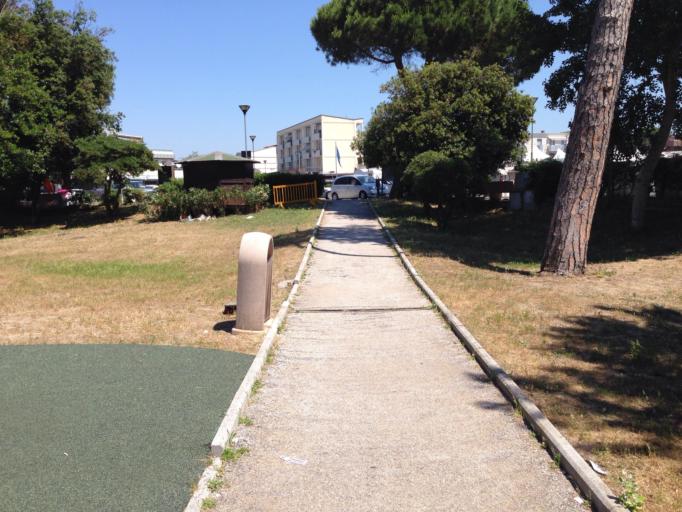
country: IT
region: Tuscany
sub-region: Province of Pisa
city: Marina di Pisa-Tirrenia-Calambrone
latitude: 43.6268
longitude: 10.2913
